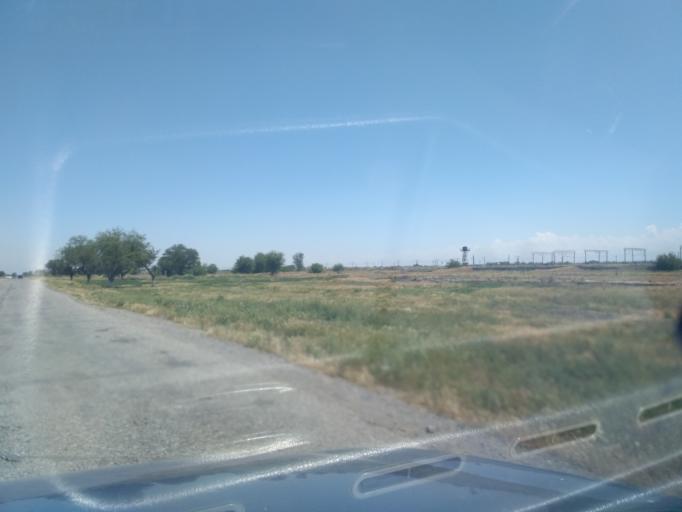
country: TJ
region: Viloyati Sughd
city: Zafarobod
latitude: 40.2151
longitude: 68.8759
